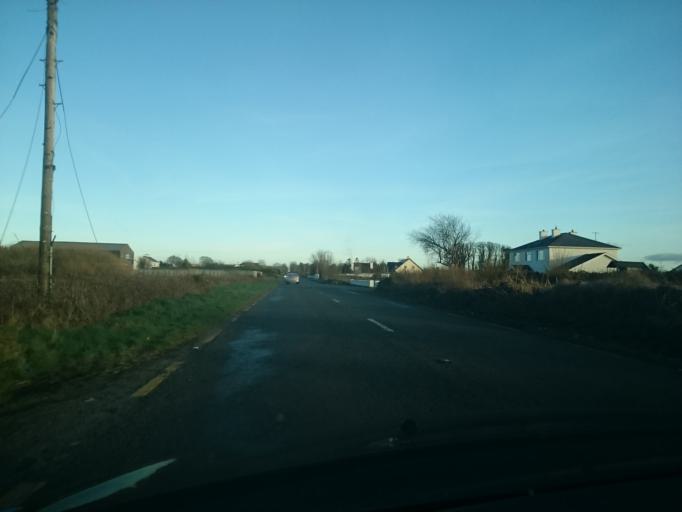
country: IE
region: Connaught
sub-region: Maigh Eo
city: Claremorris
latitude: 53.7548
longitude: -9.0345
